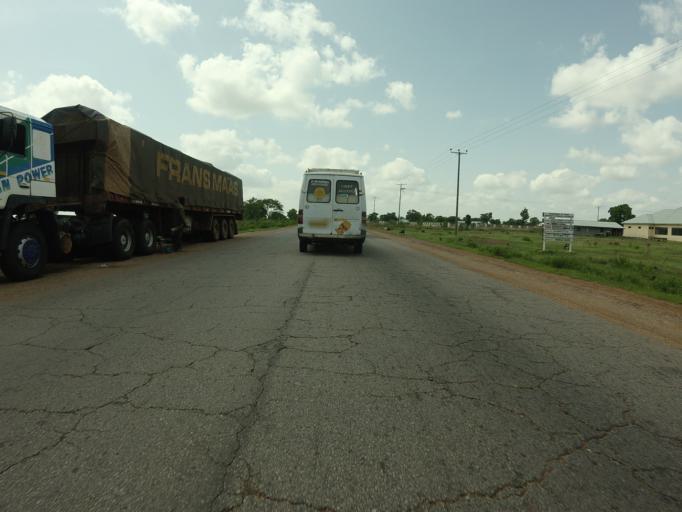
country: GH
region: Northern
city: Savelugu
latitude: 9.5857
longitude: -0.8331
